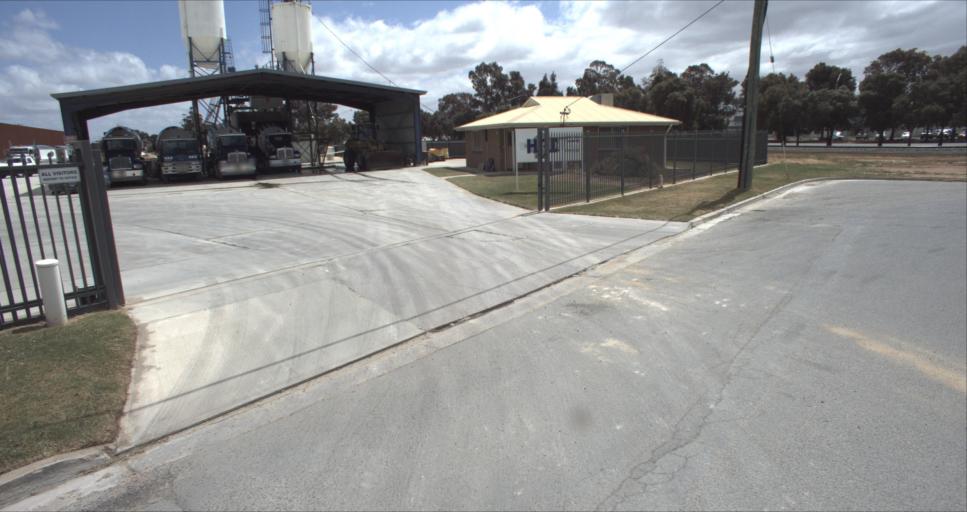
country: AU
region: New South Wales
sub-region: Leeton
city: Leeton
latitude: -34.5519
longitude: 146.3879
